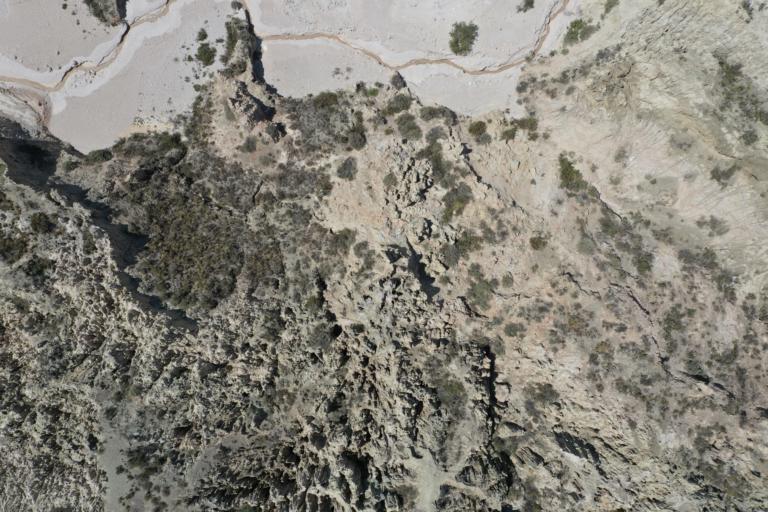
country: BO
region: La Paz
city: La Paz
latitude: -16.5620
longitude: -68.1136
